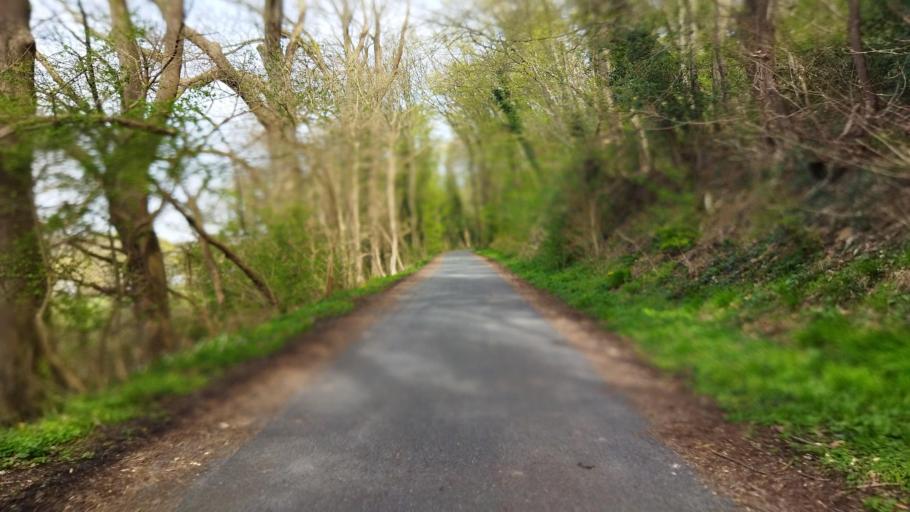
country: DE
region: North Rhine-Westphalia
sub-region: Regierungsbezirk Detmold
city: Vlotho
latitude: 52.1966
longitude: 8.8645
